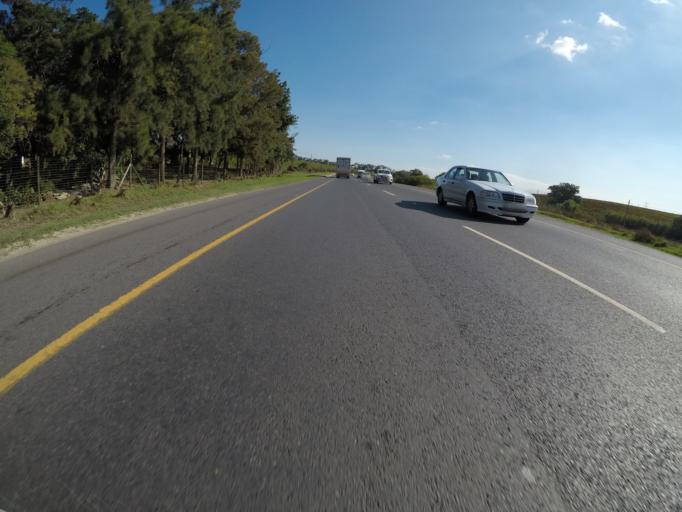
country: ZA
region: Western Cape
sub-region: City of Cape Town
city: Kraaifontein
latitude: -33.8966
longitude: 18.7339
